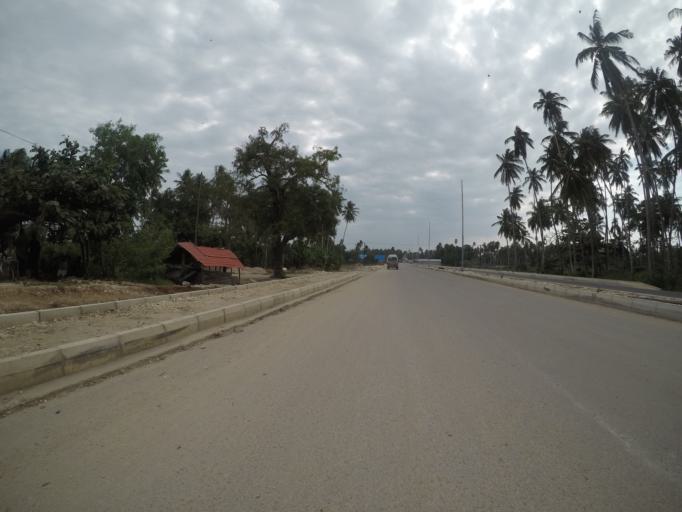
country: TZ
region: Zanzibar Central/South
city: Koani
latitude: -6.1960
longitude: 39.2772
